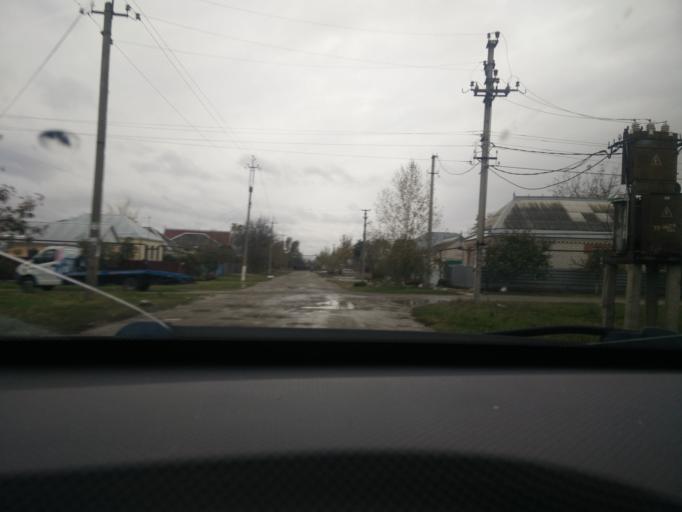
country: RU
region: Stavropol'skiy
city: Ivanovskoye
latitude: 44.5722
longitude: 41.8771
